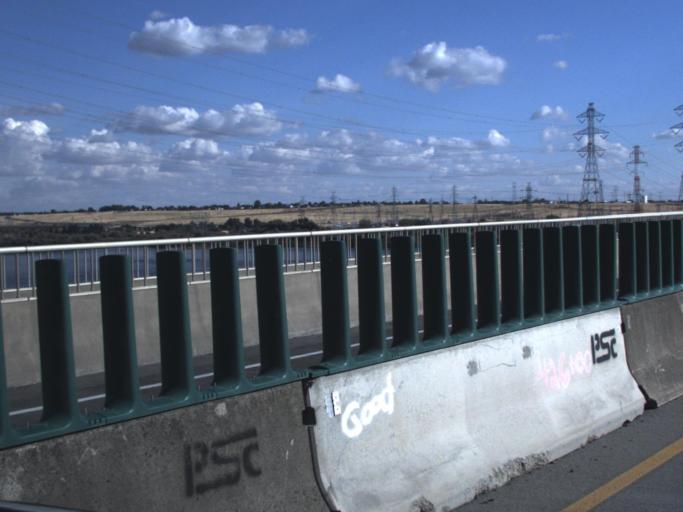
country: US
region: Oregon
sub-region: Umatilla County
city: Umatilla
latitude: 45.9347
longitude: -119.3301
